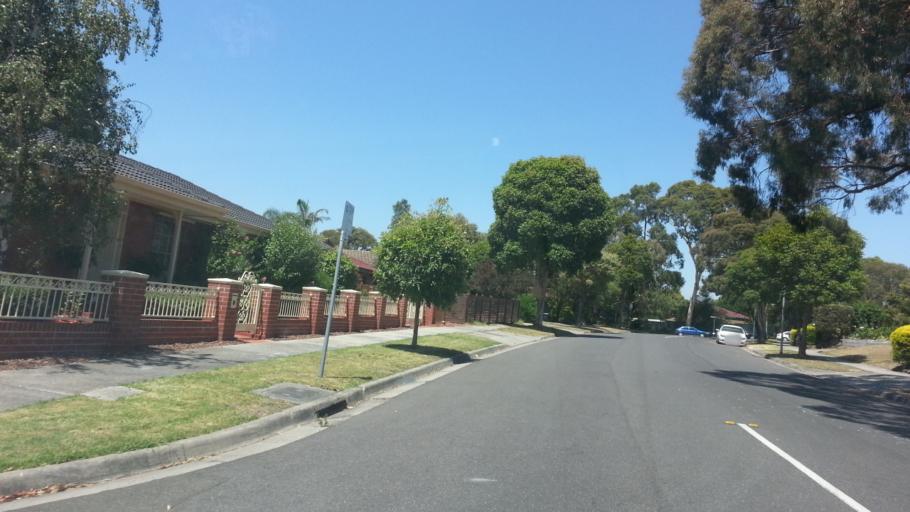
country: AU
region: Victoria
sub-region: Knox
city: Wantirna
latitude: -37.8516
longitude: 145.2304
